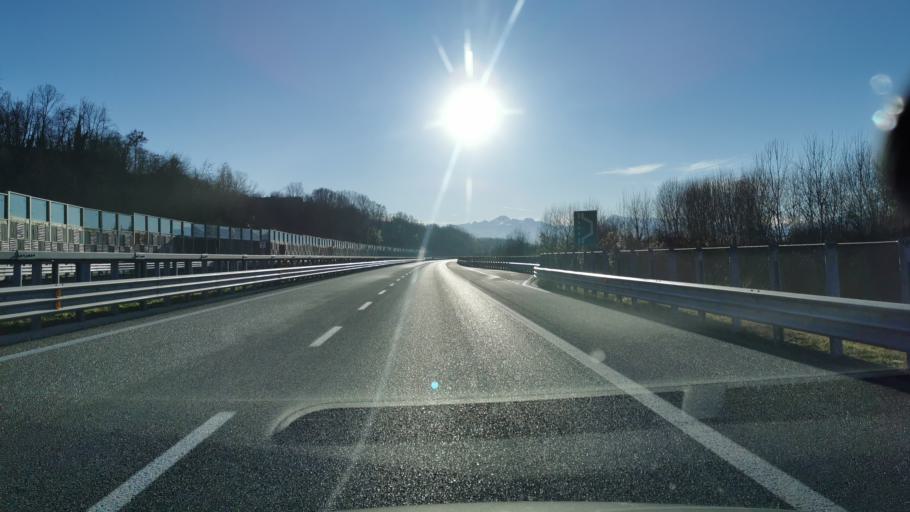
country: IT
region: Piedmont
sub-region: Provincia di Cuneo
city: Montanera
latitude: 44.4636
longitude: 7.6630
